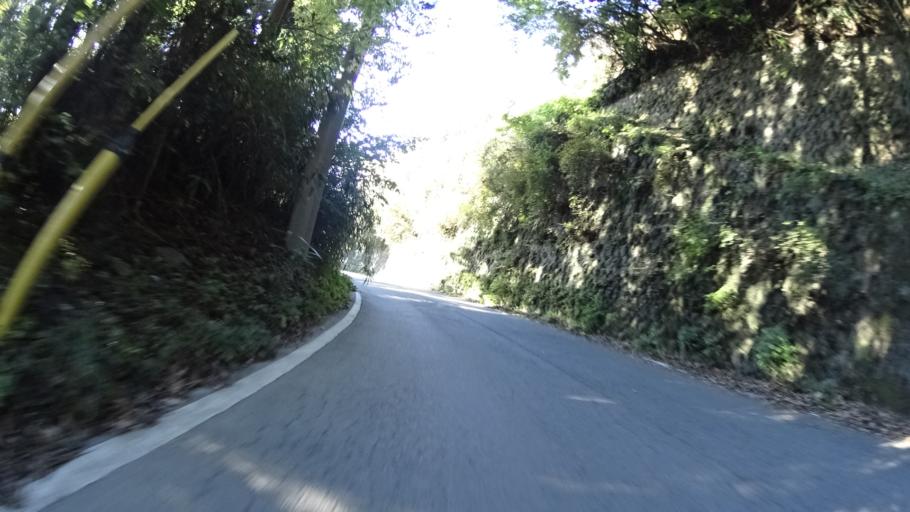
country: JP
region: Yamanashi
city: Uenohara
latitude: 35.6781
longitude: 139.0921
